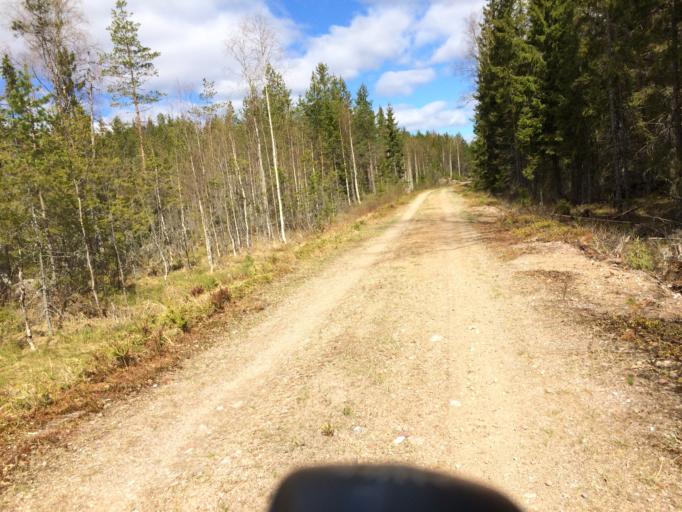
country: SE
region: OErebro
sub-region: Hallefors Kommun
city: Haellefors
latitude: 60.0548
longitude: 14.5232
